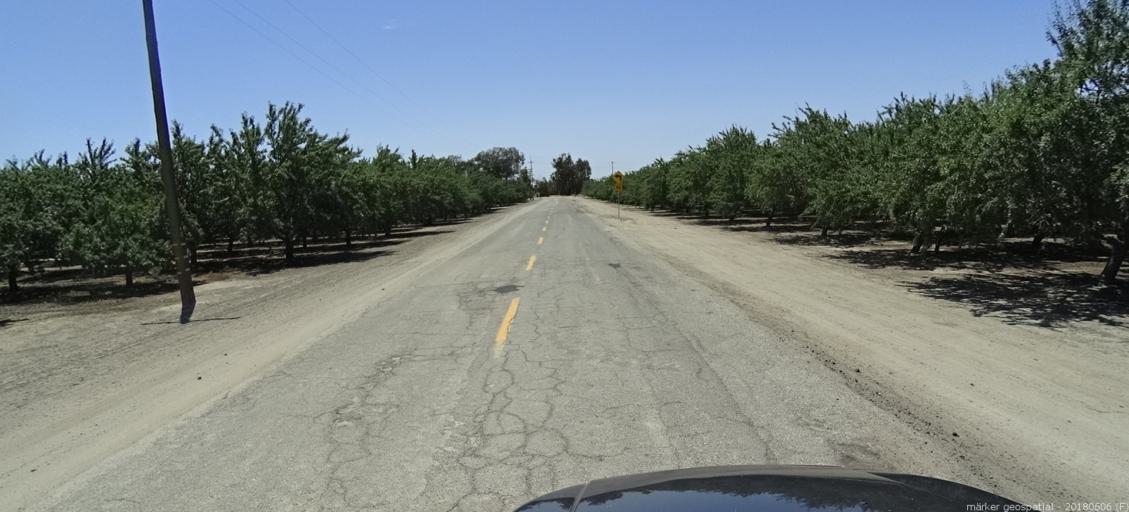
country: US
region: California
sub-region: Fresno County
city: Firebaugh
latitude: 36.8452
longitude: -120.4179
